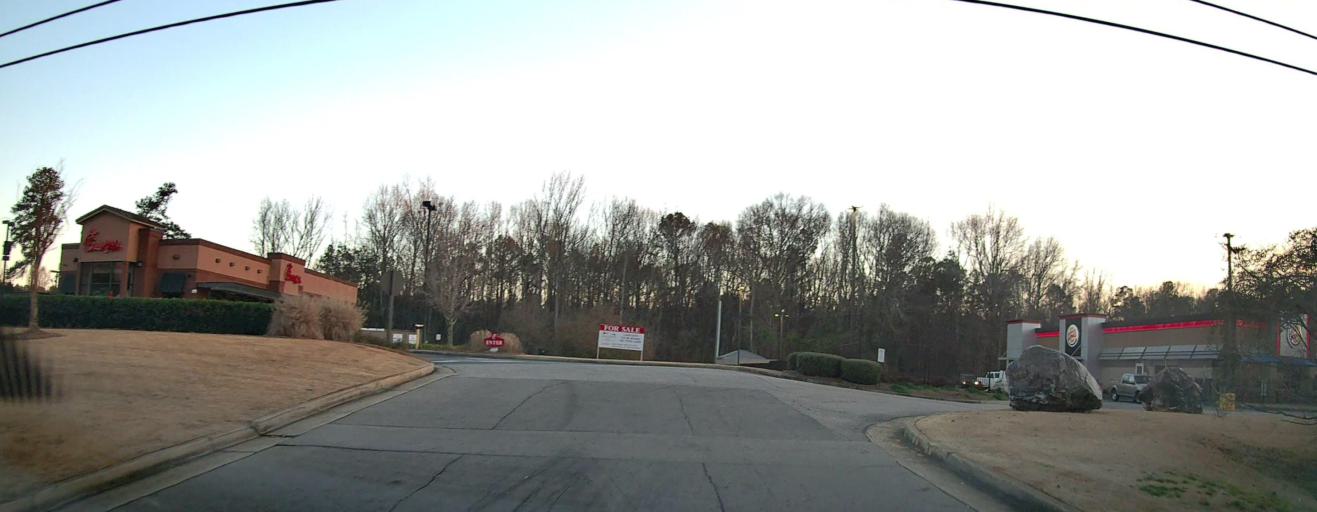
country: US
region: Georgia
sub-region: Troup County
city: La Grange
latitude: 33.0419
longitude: -84.9750
